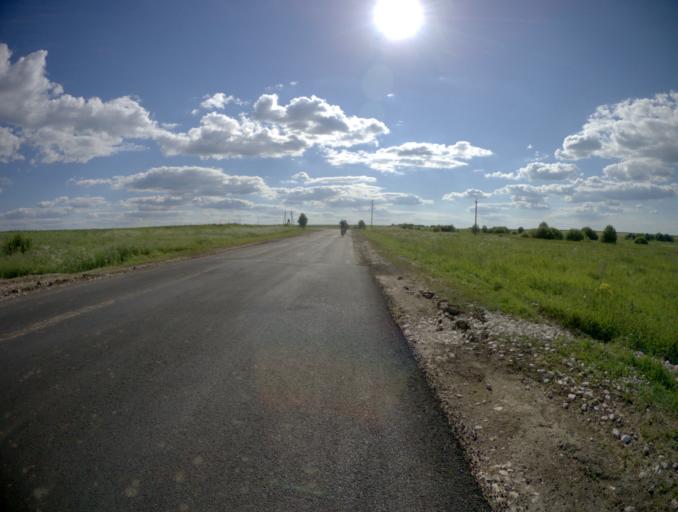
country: RU
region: Vladimir
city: Suzdal'
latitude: 56.3410
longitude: 40.3224
